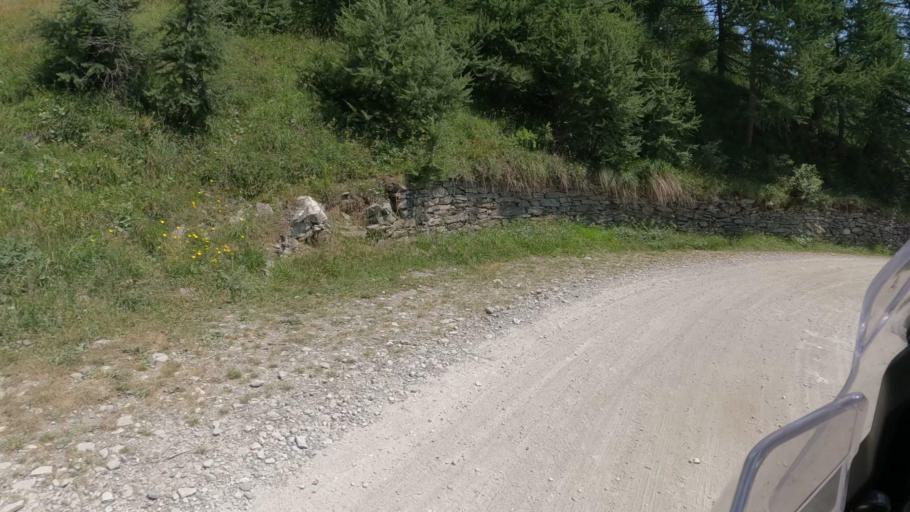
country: IT
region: Piedmont
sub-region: Provincia di Torino
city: Fenestrelle
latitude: 45.0577
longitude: 7.0505
